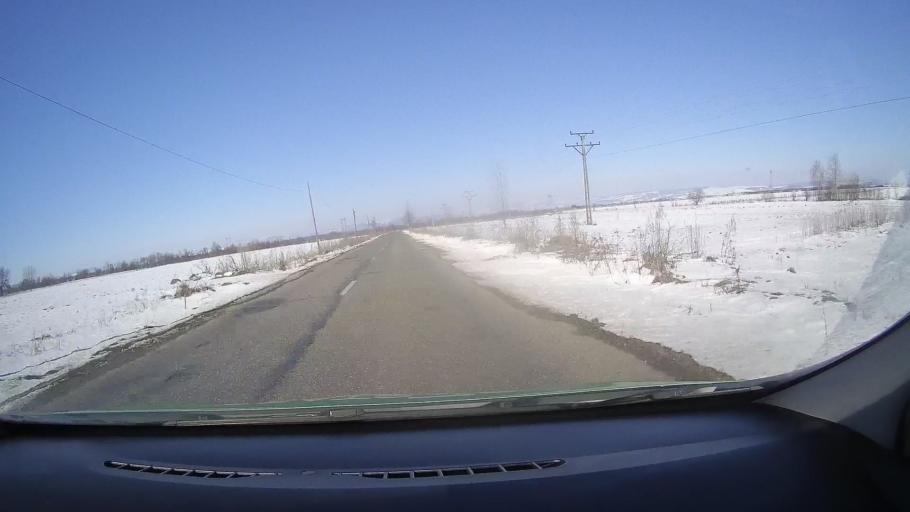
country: RO
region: Brasov
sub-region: Comuna Harseni
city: Harseni
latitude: 45.7690
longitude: 25.0031
